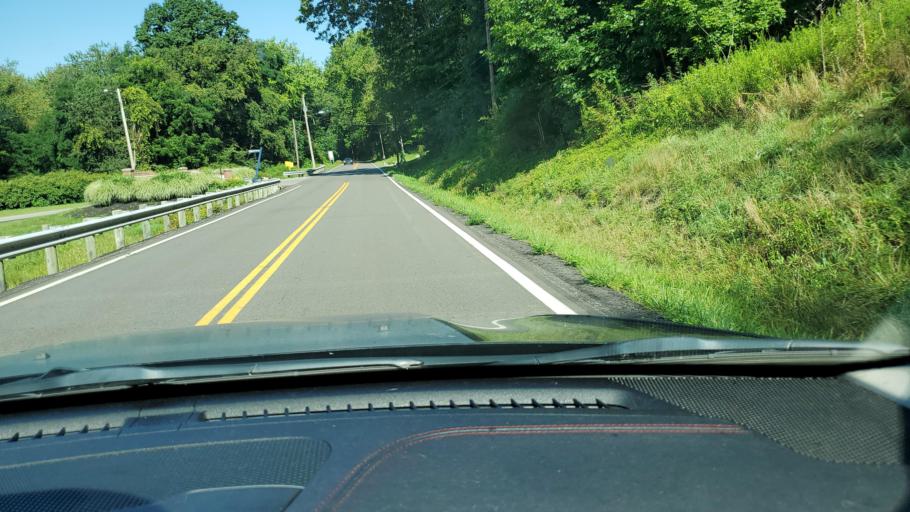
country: US
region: Ohio
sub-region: Mahoning County
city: Lowellville
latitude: 41.0470
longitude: -80.5560
